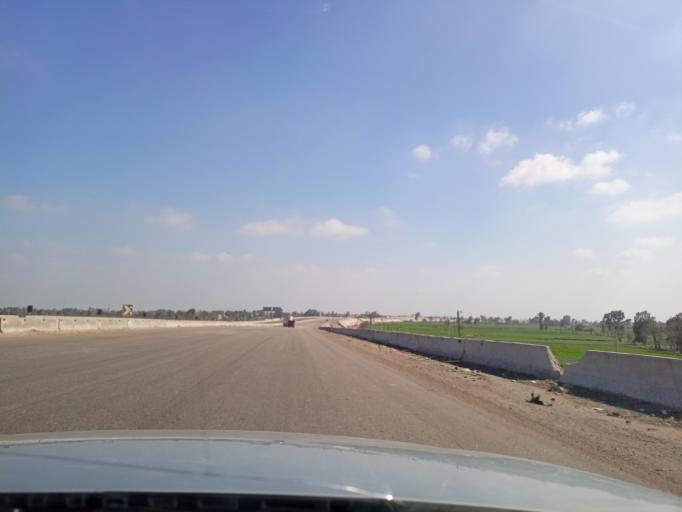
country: EG
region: Eastern Province
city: Mashtul as Suq
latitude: 30.4625
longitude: 31.3680
